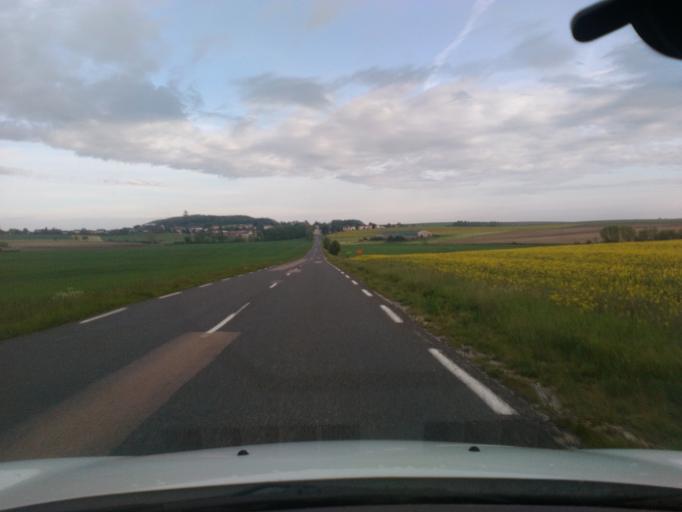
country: FR
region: Champagne-Ardenne
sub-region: Departement de la Haute-Marne
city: Lavilleneuve-au-Roi
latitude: 48.2167
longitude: 4.9068
